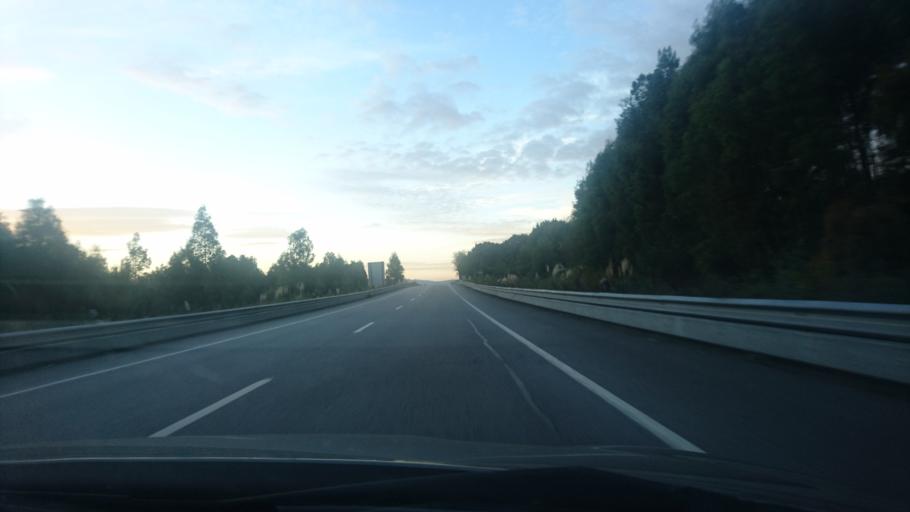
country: PT
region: Aveiro
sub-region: Santa Maria da Feira
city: Arrifana
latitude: 40.9180
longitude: -8.4892
